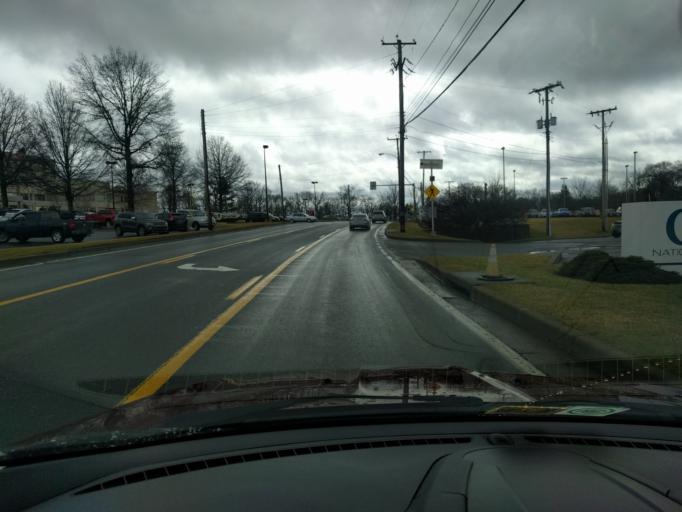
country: US
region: West Virginia
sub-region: Raleigh County
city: Mabscott
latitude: 37.7881
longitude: -81.2035
